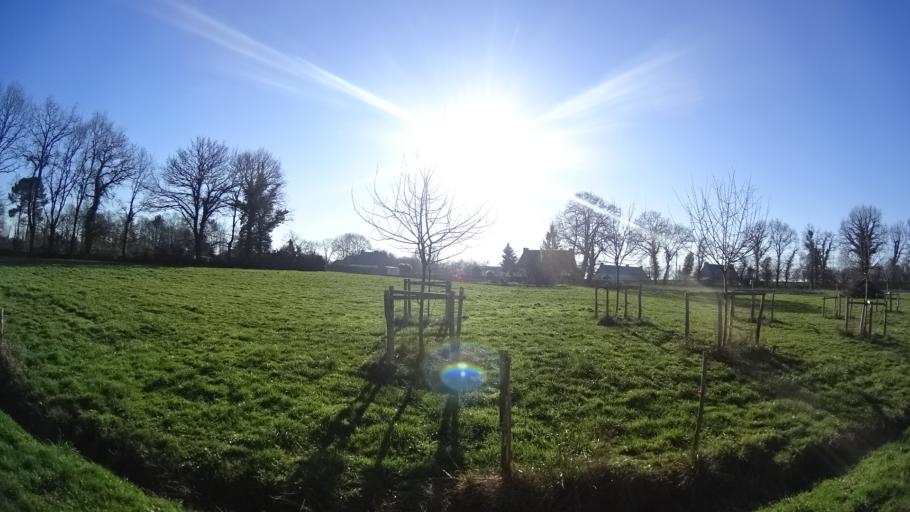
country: FR
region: Brittany
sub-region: Departement du Morbihan
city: Saint-Jean-la-Poterie
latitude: 47.6479
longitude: -2.1346
